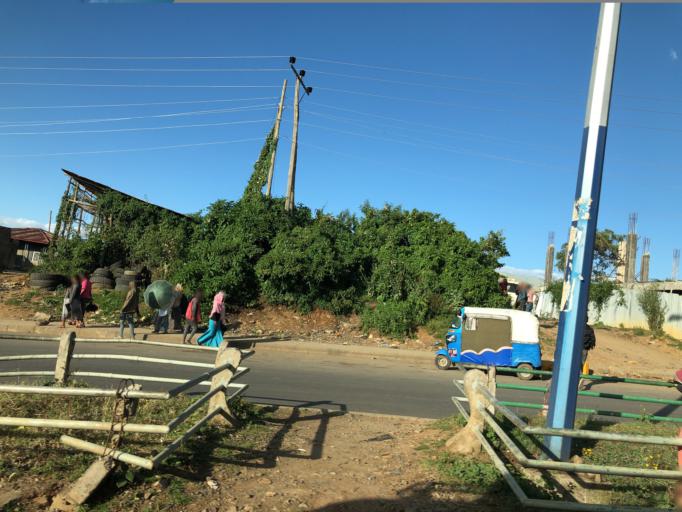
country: ET
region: Amhara
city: Debre Tabor
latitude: 11.8588
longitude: 38.0026
